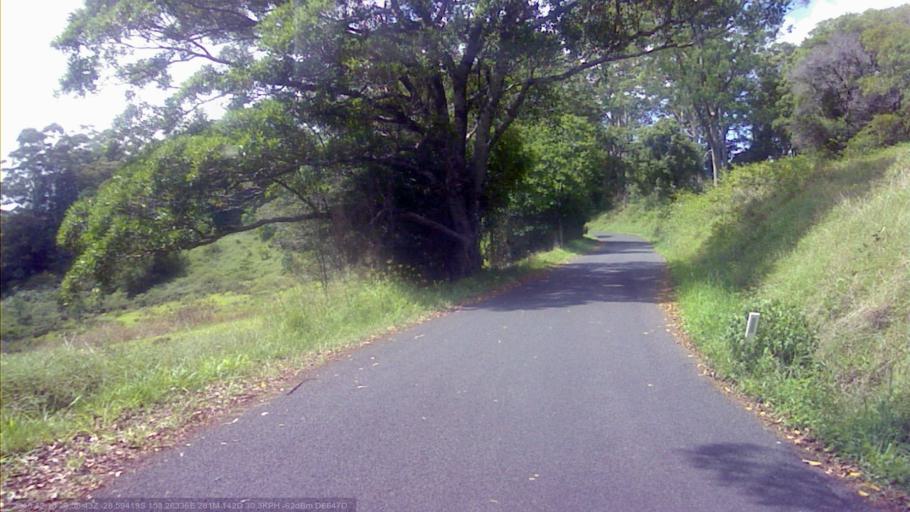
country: AU
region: New South Wales
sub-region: Lismore Municipality
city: Nimbin
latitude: -28.5942
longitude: 153.2634
